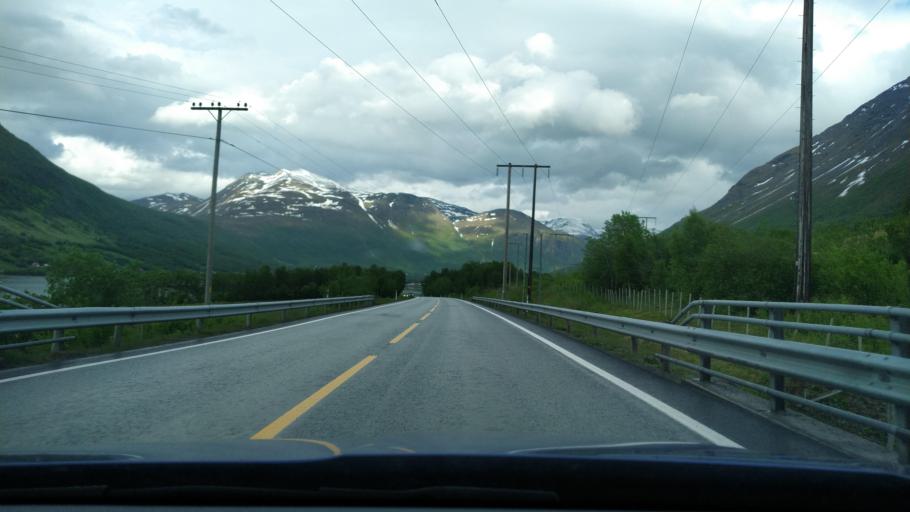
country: NO
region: Troms
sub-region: Balsfjord
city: Storsteinnes
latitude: 69.2150
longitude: 19.4880
